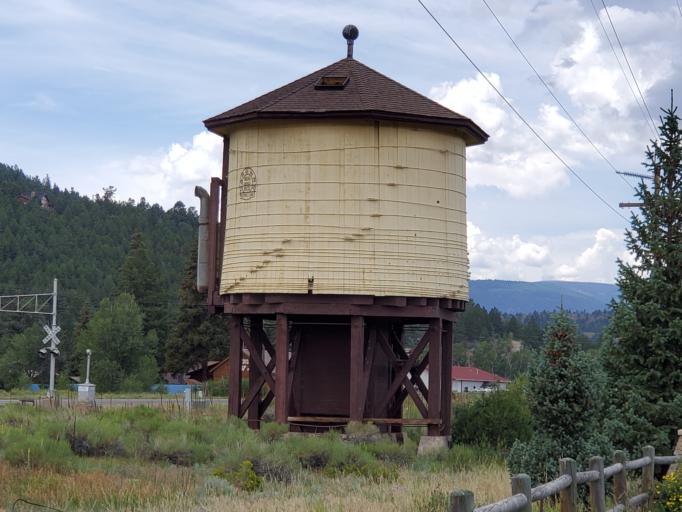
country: US
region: Colorado
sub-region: Rio Grande County
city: Del Norte
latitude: 37.6720
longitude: -106.6257
